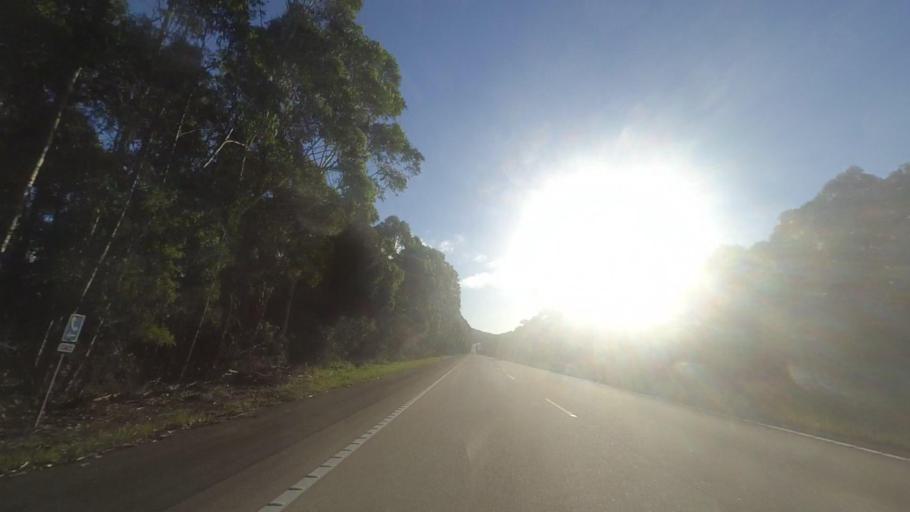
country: AU
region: New South Wales
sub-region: Great Lakes
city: Bulahdelah
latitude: -32.3779
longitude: 152.2732
